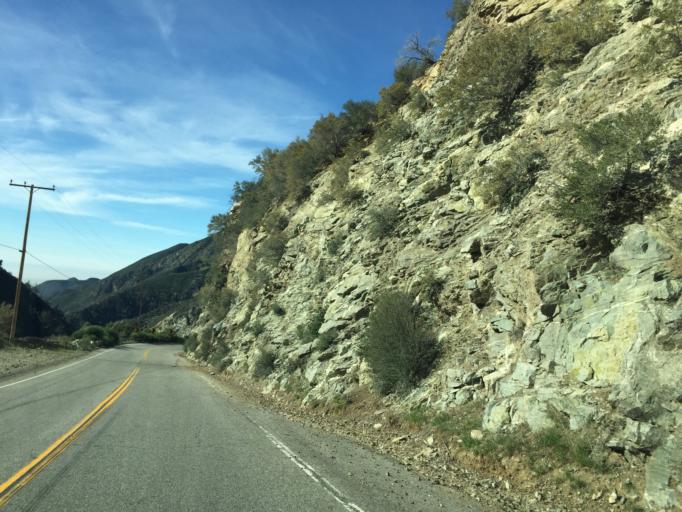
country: US
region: California
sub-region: San Bernardino County
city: San Antonio Heights
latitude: 34.2181
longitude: -117.6710
